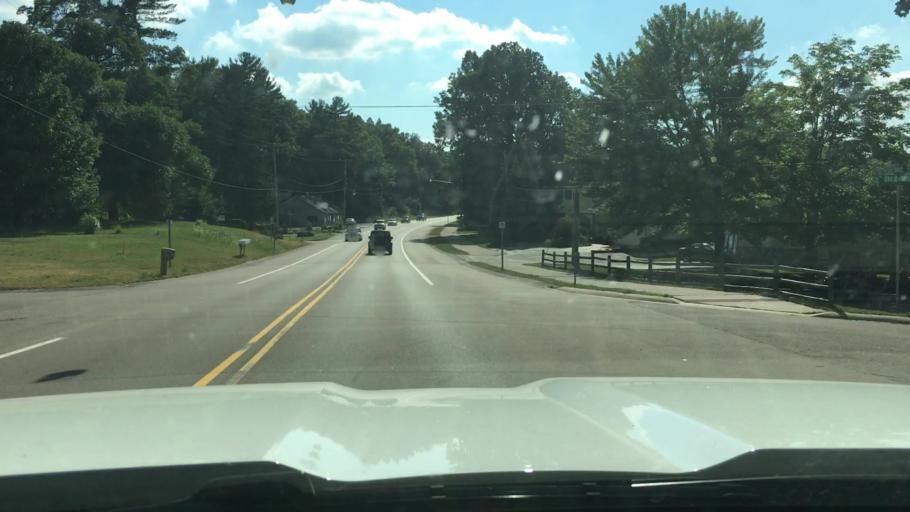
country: US
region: Michigan
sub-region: Kent County
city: Rockford
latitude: 43.0846
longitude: -85.4537
